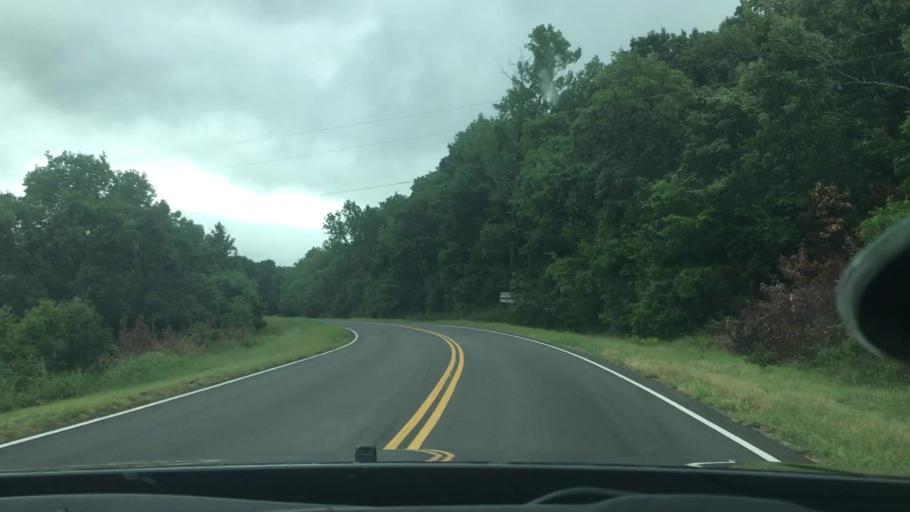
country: US
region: Oklahoma
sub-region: Sequoyah County
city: Vian
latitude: 35.6610
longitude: -94.9493
